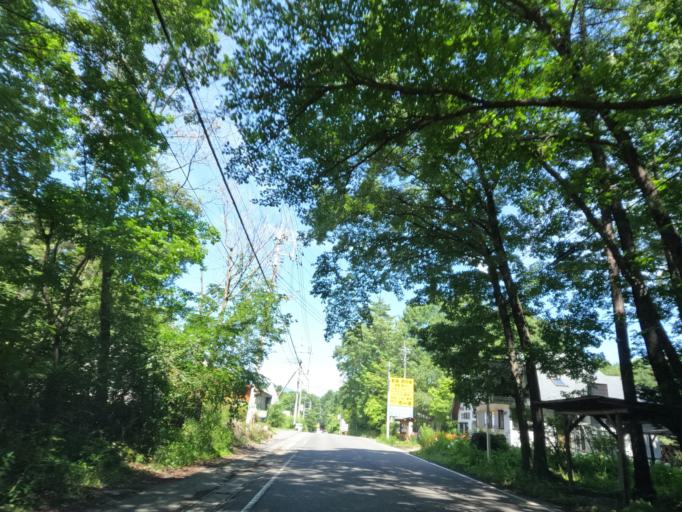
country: JP
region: Nagano
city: Komoro
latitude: 36.4683
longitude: 138.5670
